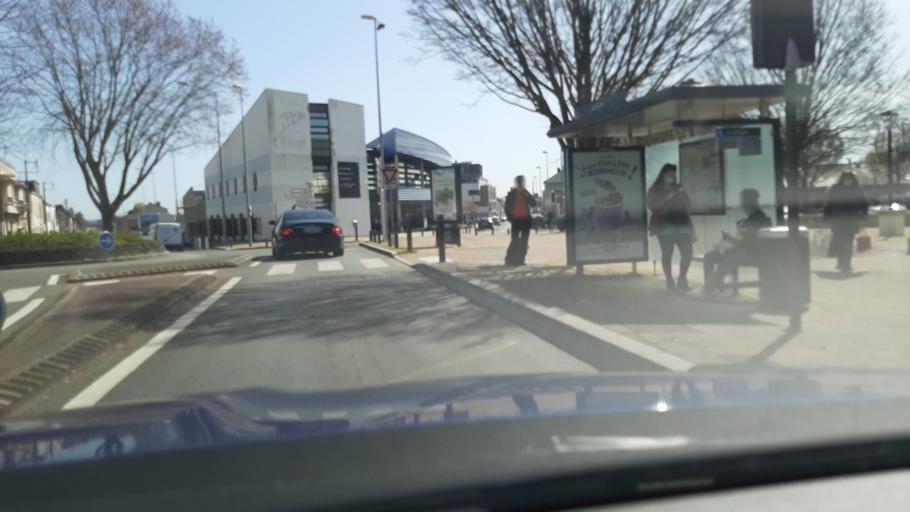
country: FR
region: Pays de la Loire
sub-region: Departement de Maine-et-Loire
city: Angers
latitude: 47.4534
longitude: -0.5263
